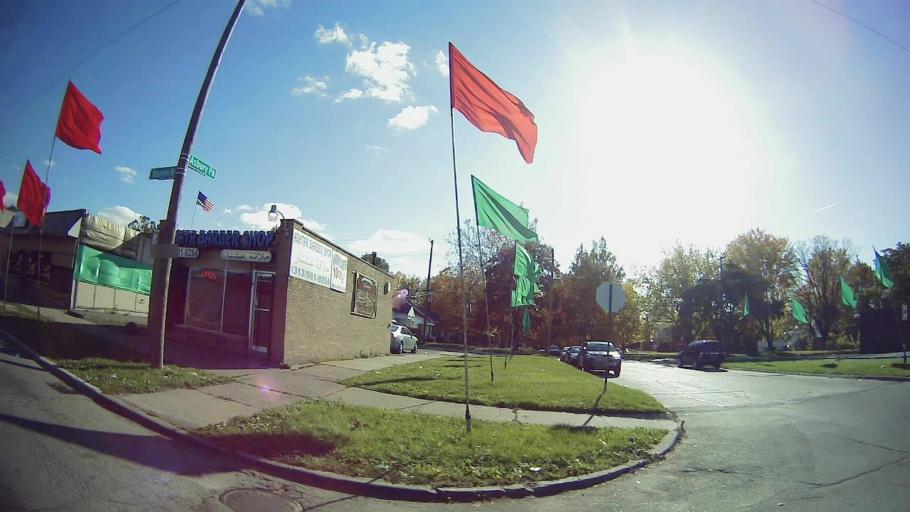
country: US
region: Michigan
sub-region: Wayne County
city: Dearborn
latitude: 42.3435
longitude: -83.2062
